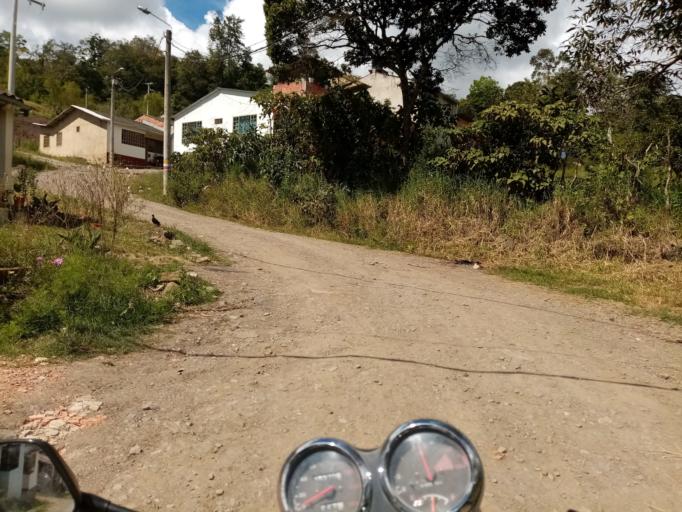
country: CO
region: Cundinamarca
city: Tenza
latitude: 5.0941
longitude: -73.4458
